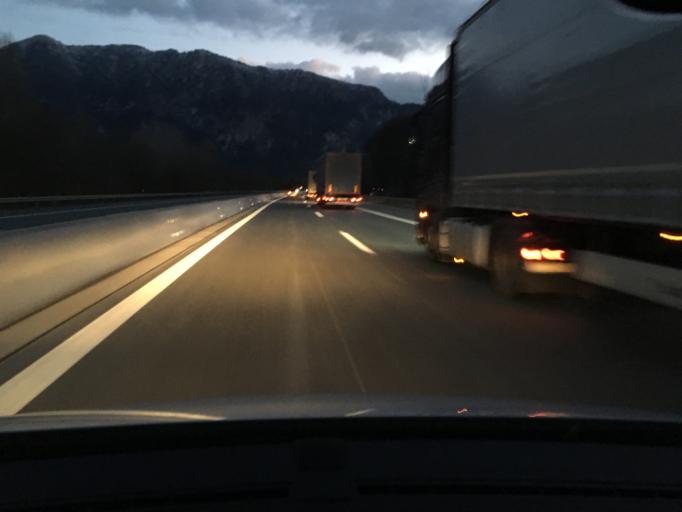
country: AT
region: Tyrol
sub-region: Politischer Bezirk Kufstein
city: Ebbs
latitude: 47.6289
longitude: 12.2001
